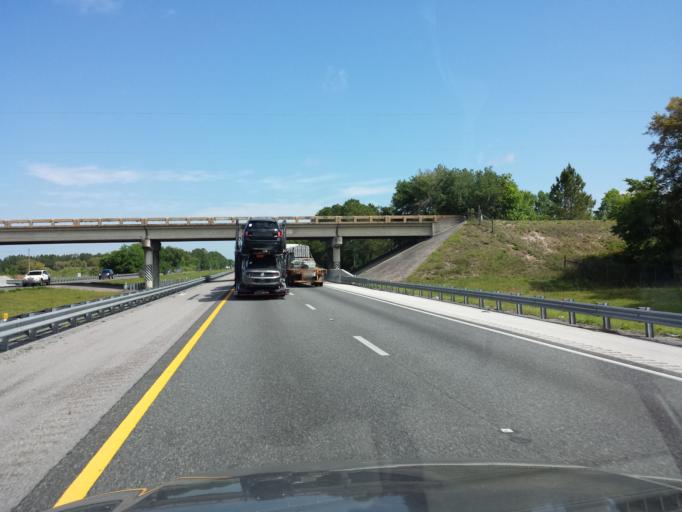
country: US
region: Florida
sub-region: Sumter County
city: Lake Panasoffkee
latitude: 28.7993
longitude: -82.0879
